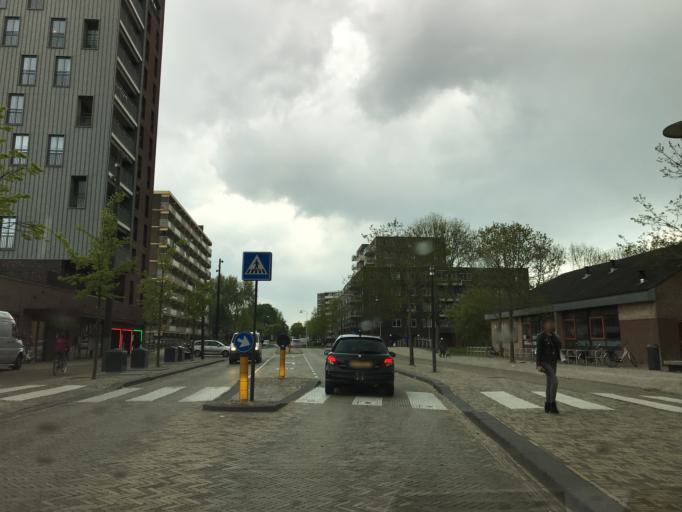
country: NL
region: North Holland
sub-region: Gemeente Diemen
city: Diemen
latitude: 52.3422
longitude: 4.9645
